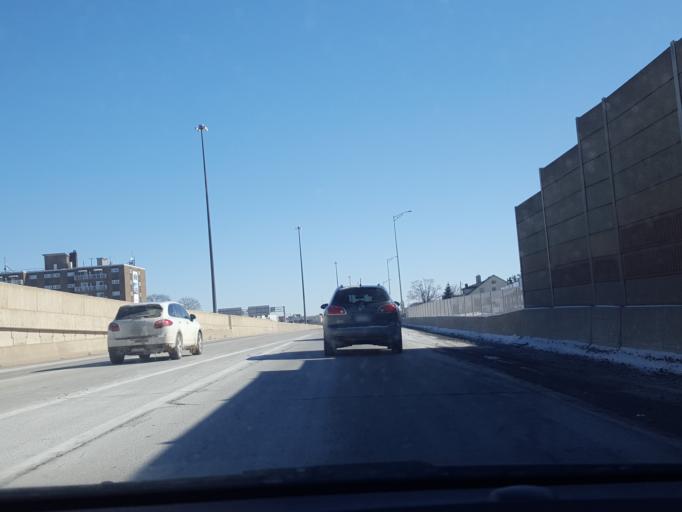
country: CA
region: Ontario
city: Kitchener
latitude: 43.4353
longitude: -80.4546
